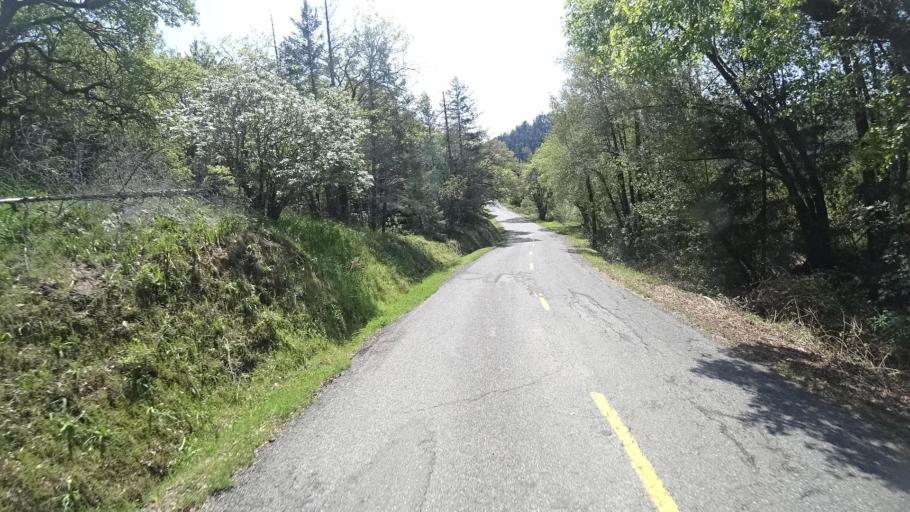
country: US
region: California
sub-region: Humboldt County
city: Redway
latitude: 40.2675
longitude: -123.6257
